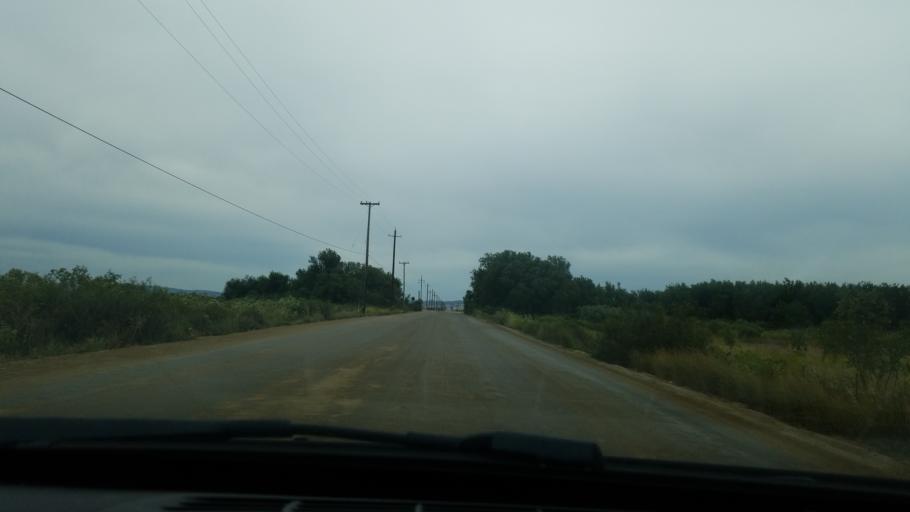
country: US
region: California
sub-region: Santa Barbara County
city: Guadalupe
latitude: 34.9824
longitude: -120.5130
